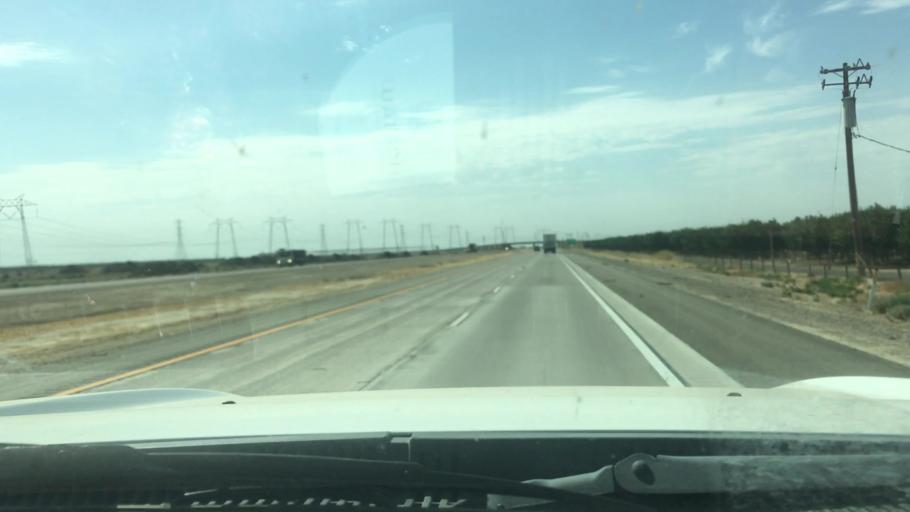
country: US
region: California
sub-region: Kern County
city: Buttonwillow
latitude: 35.5077
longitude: -119.5435
